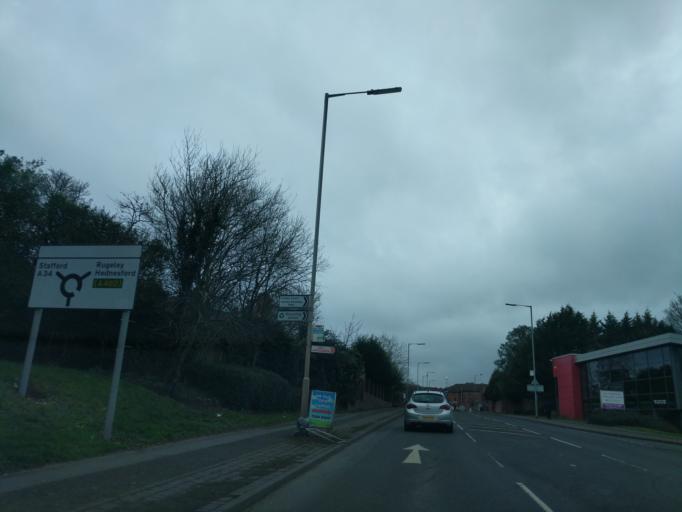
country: GB
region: England
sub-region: Staffordshire
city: Cannock
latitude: 52.6882
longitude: -2.0238
